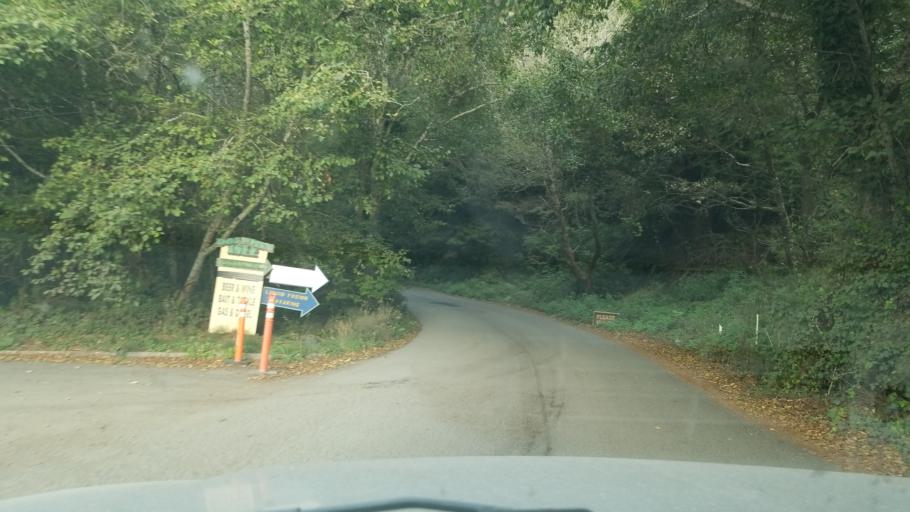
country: US
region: California
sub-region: Mendocino County
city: Fort Bragg
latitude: 39.4269
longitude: -123.7969
